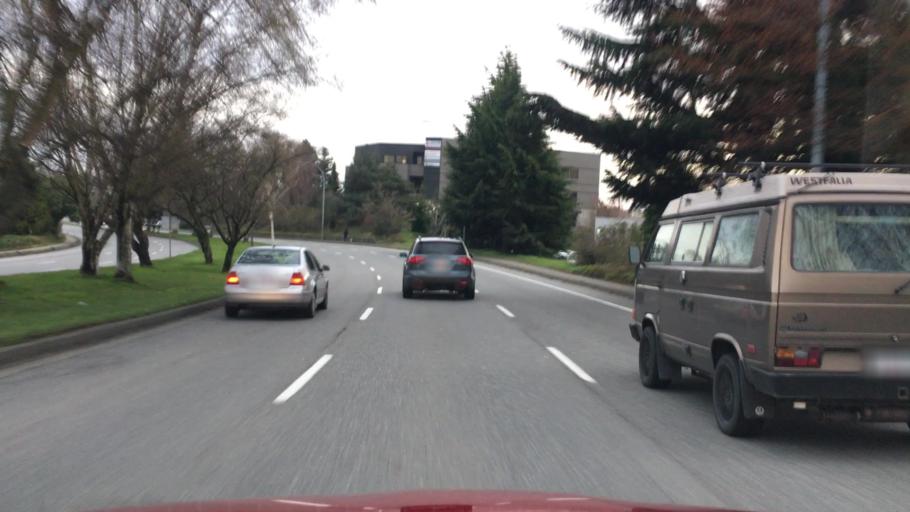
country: CA
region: British Columbia
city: Victoria
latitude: 48.4533
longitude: -123.3714
